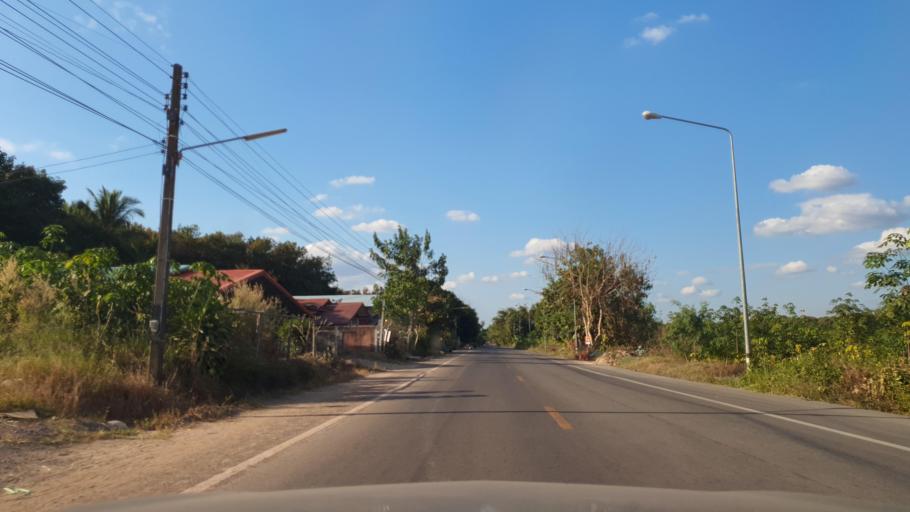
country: TH
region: Nong Khai
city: Bueng Khong Long
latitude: 17.9995
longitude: 104.0157
